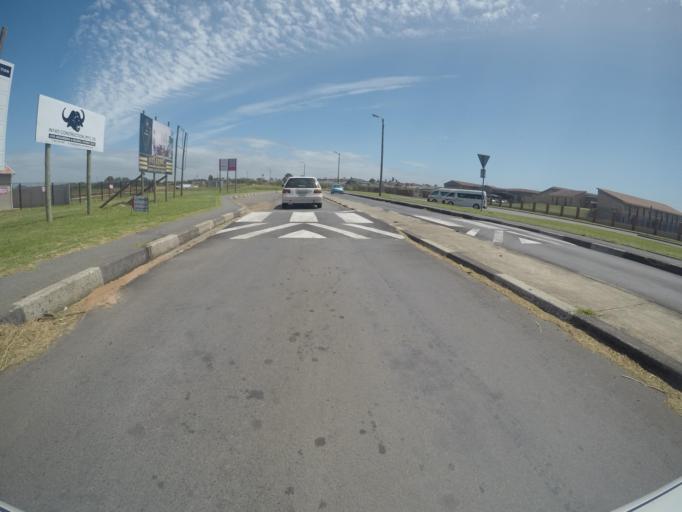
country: ZA
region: Eastern Cape
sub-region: Buffalo City Metropolitan Municipality
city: East London
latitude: -32.9474
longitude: 27.9962
